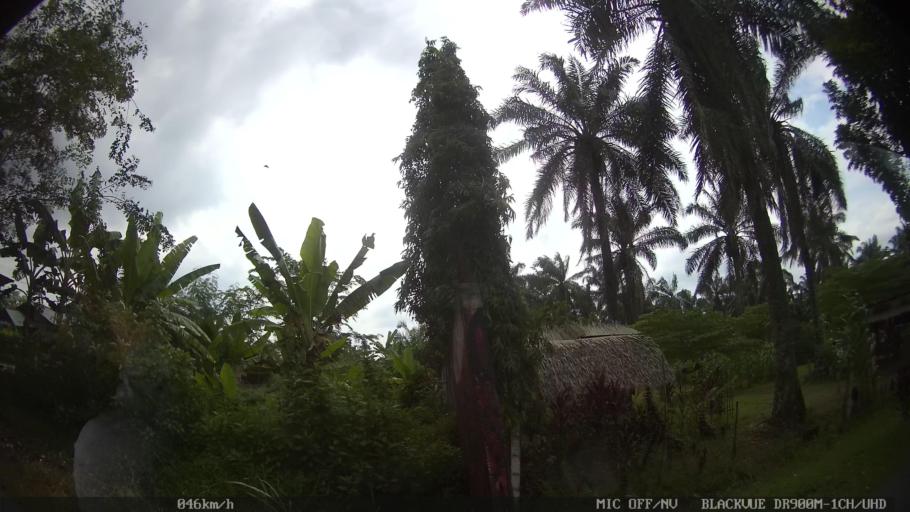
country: ID
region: North Sumatra
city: Sunggal
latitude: 3.6278
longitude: 98.6061
